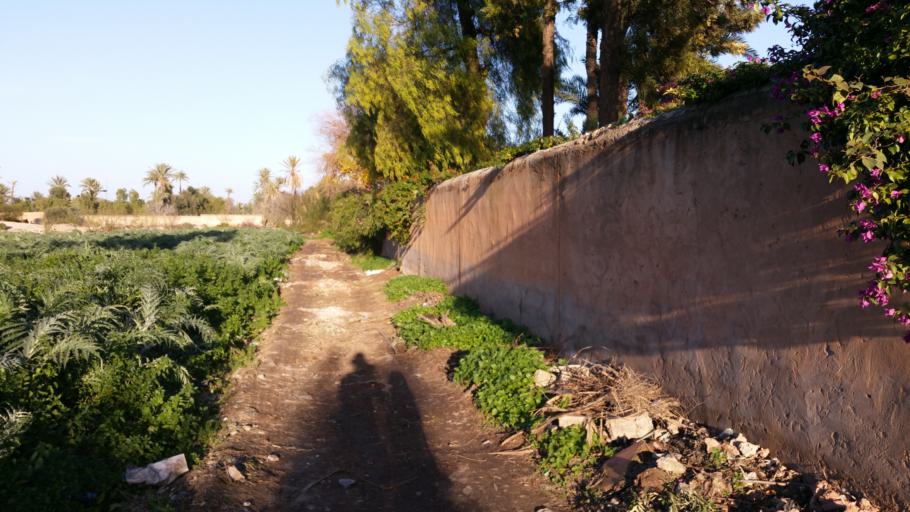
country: MA
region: Marrakech-Tensift-Al Haouz
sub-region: Marrakech
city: Marrakesh
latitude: 31.6552
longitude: -7.9799
